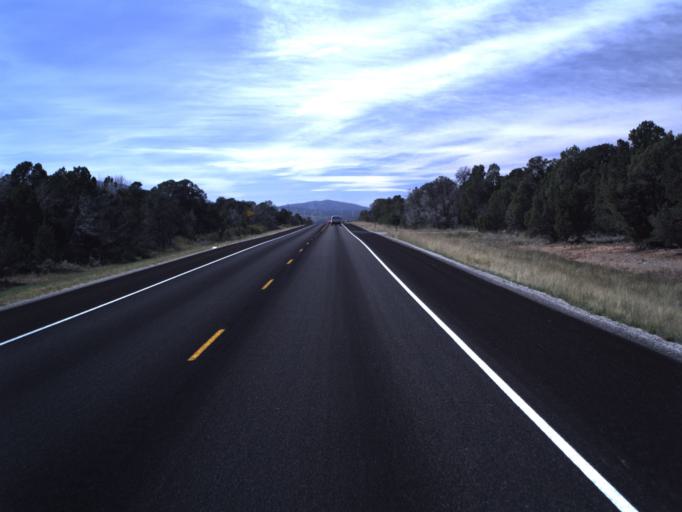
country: US
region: Utah
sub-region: San Juan County
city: Monticello
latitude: 37.8586
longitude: -109.2015
